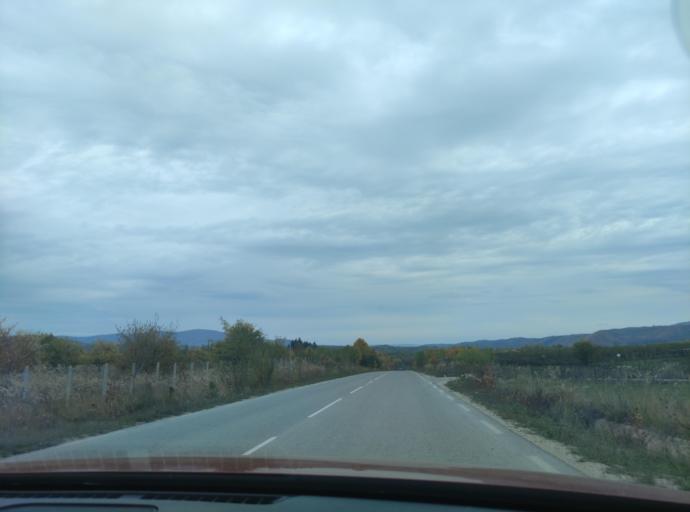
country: BG
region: Montana
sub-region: Obshtina Berkovitsa
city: Berkovitsa
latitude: 43.2270
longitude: 23.1573
